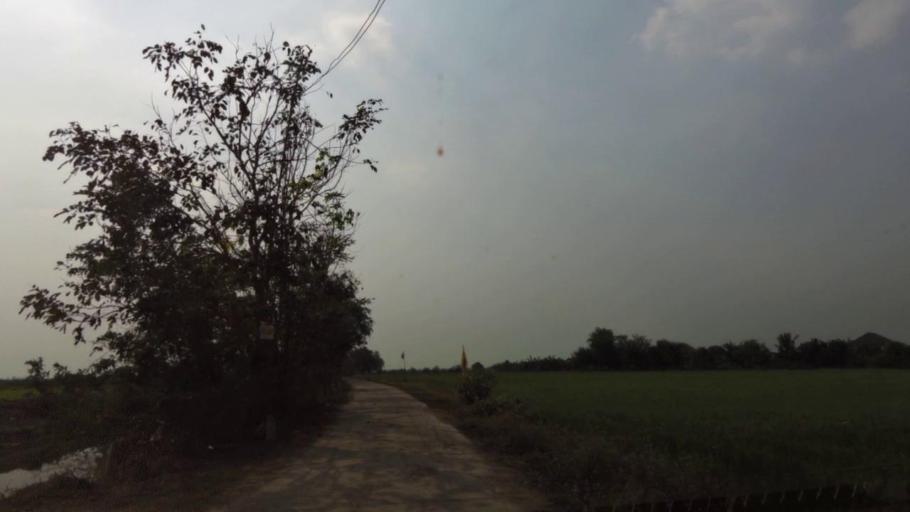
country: TH
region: Phra Nakhon Si Ayutthaya
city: Phra Nakhon Si Ayutthaya
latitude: 14.3153
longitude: 100.5608
